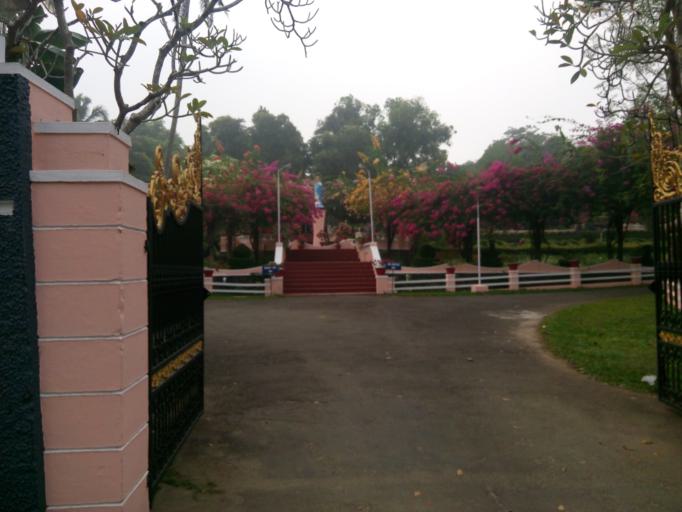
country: IN
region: Kerala
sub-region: Kottayam
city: Lalam
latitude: 9.7093
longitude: 76.6745
